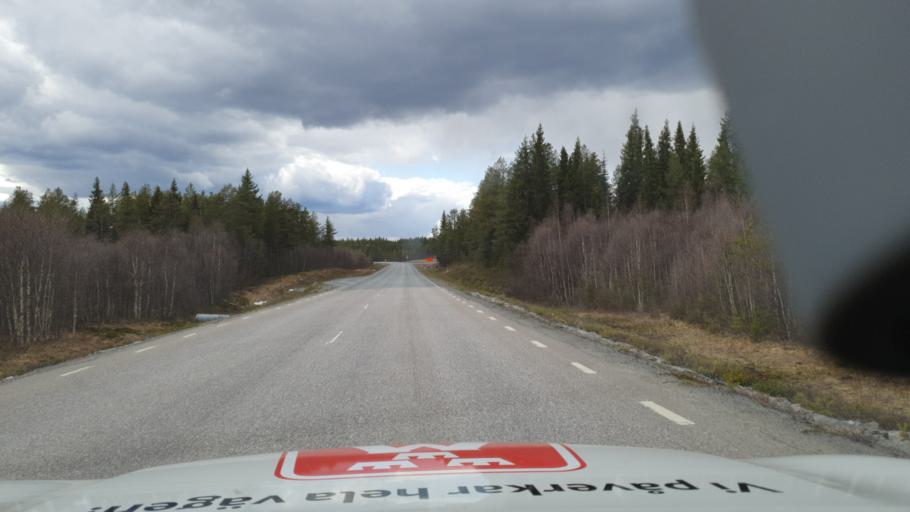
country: SE
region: Norrbotten
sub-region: Arjeplogs Kommun
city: Arjeplog
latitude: 65.5843
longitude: 18.1606
